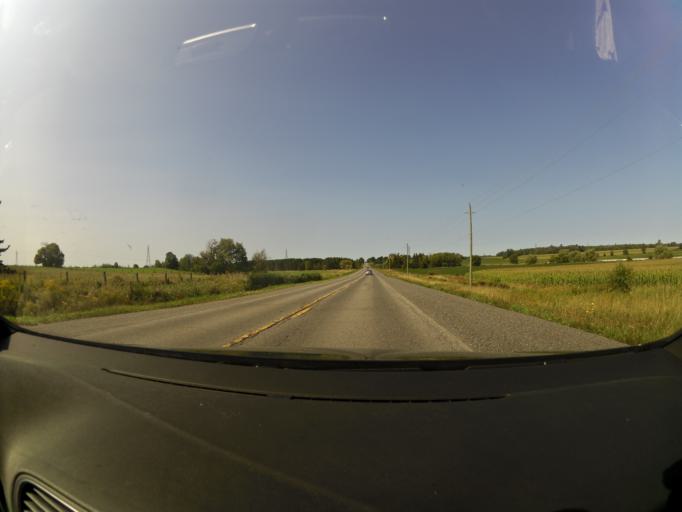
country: CA
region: Ontario
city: Arnprior
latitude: 45.3990
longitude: -76.3179
